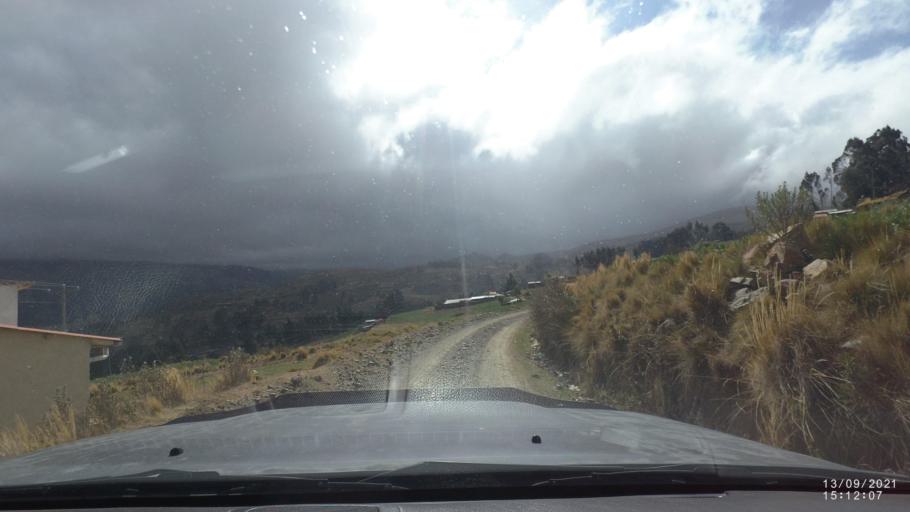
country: BO
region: Cochabamba
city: Colomi
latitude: -17.3620
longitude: -65.8057
